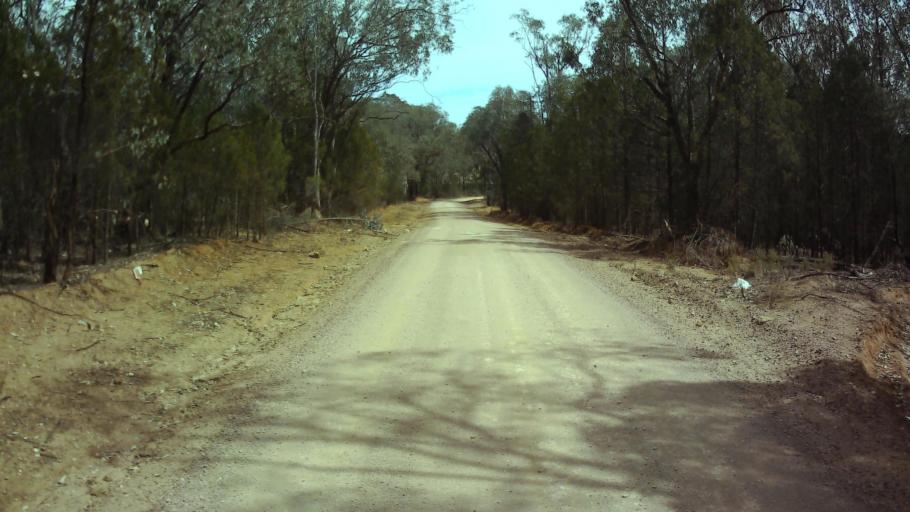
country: AU
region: New South Wales
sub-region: Weddin
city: Grenfell
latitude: -33.9200
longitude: 148.4142
